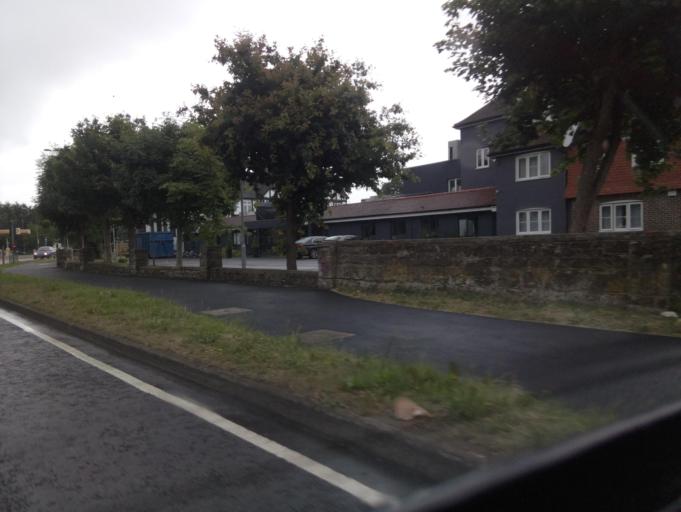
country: GB
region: England
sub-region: Surrey
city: Horley
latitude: 51.1819
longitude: -0.1635
